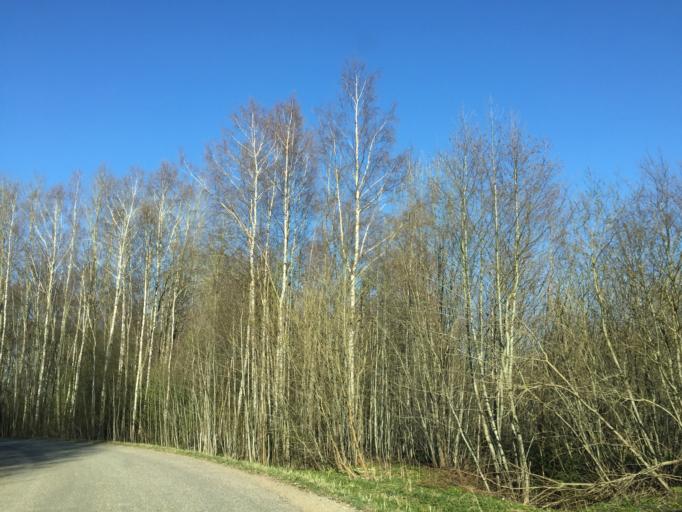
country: EE
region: Valgamaa
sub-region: Torva linn
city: Torva
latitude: 58.2319
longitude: 25.9422
